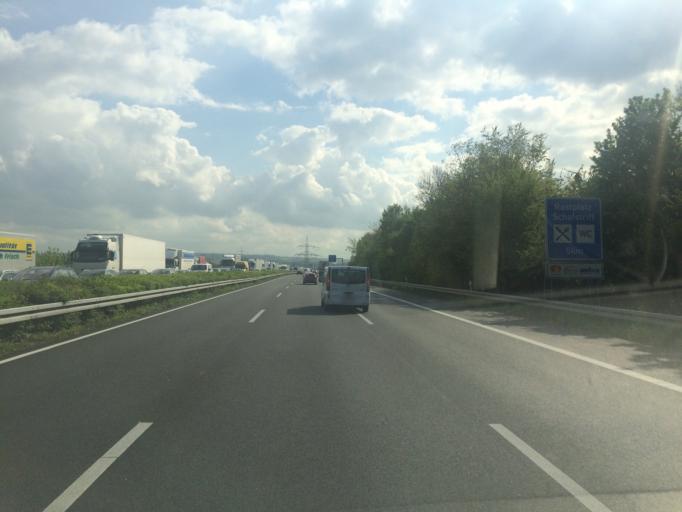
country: DE
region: Lower Saxony
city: Lauenau
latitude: 52.2926
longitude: 9.3618
